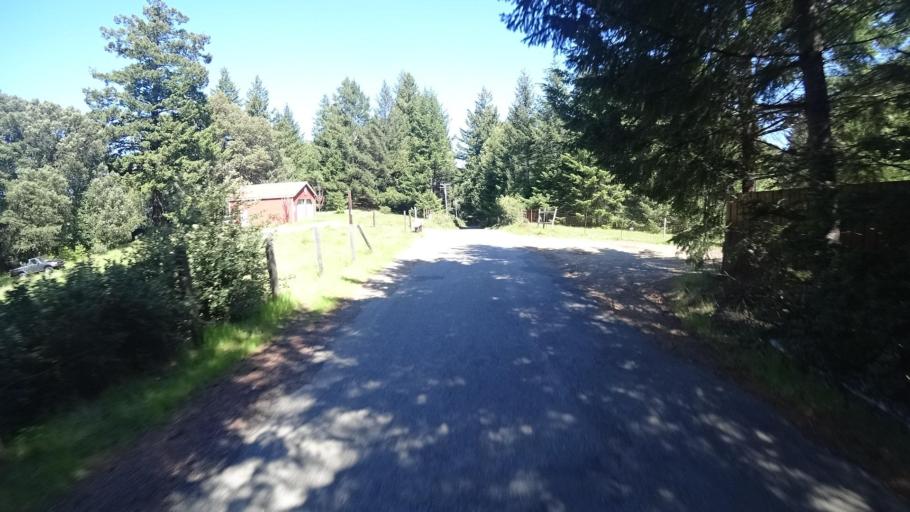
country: US
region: California
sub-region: Humboldt County
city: Redway
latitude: 40.1976
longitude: -124.1010
